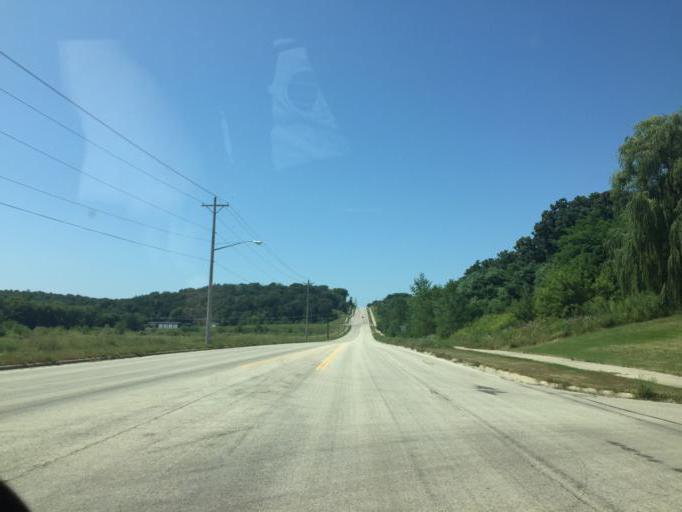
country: US
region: Minnesota
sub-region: Olmsted County
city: Rochester
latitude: 43.9639
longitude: -92.4726
